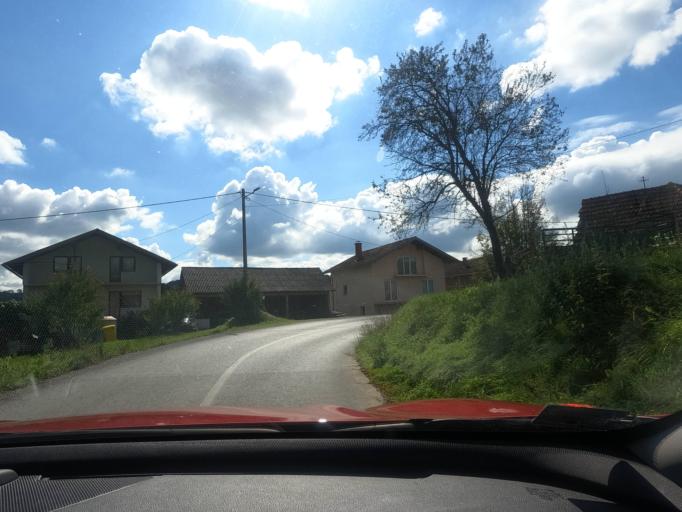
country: BA
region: Federation of Bosnia and Herzegovina
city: Velika Kladusa
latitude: 45.2138
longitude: 15.8220
